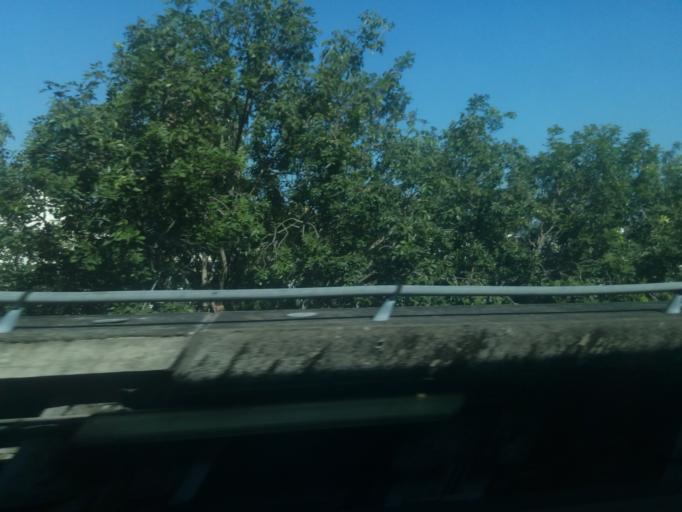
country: HK
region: Yuen Long
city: Yuen Long Kau Hui
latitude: 22.4474
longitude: 114.0303
